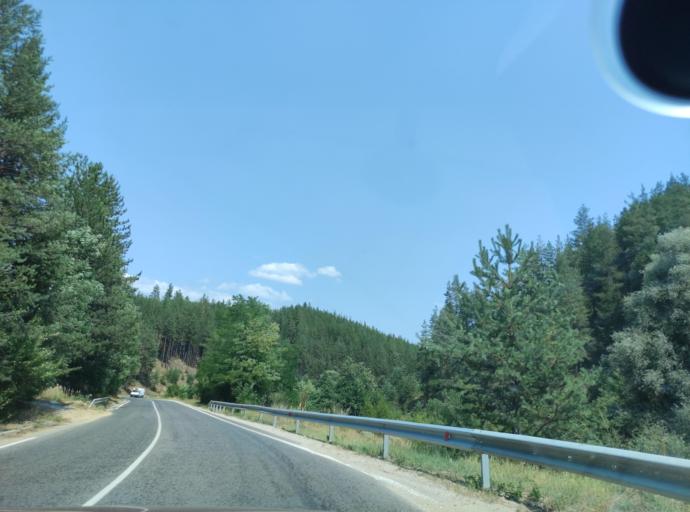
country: BG
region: Blagoevgrad
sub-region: Obshtina Razlog
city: Razlog
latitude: 41.8918
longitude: 23.5355
